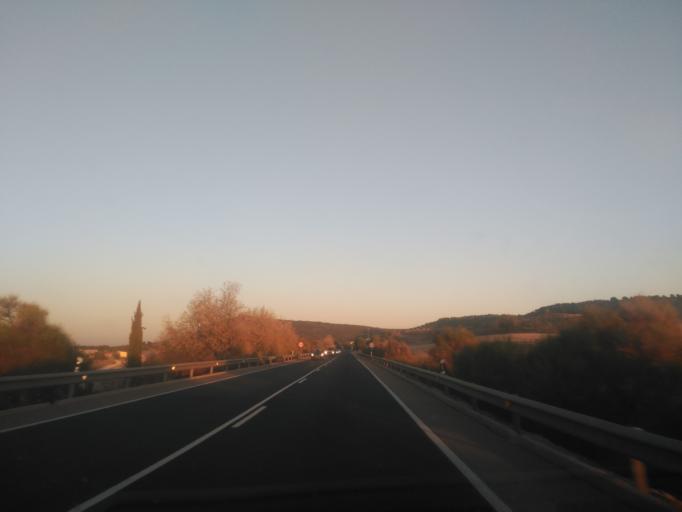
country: ES
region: Castille and Leon
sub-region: Provincia de Valladolid
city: Quintanilla de Onesimo
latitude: 41.6208
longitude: -4.3751
